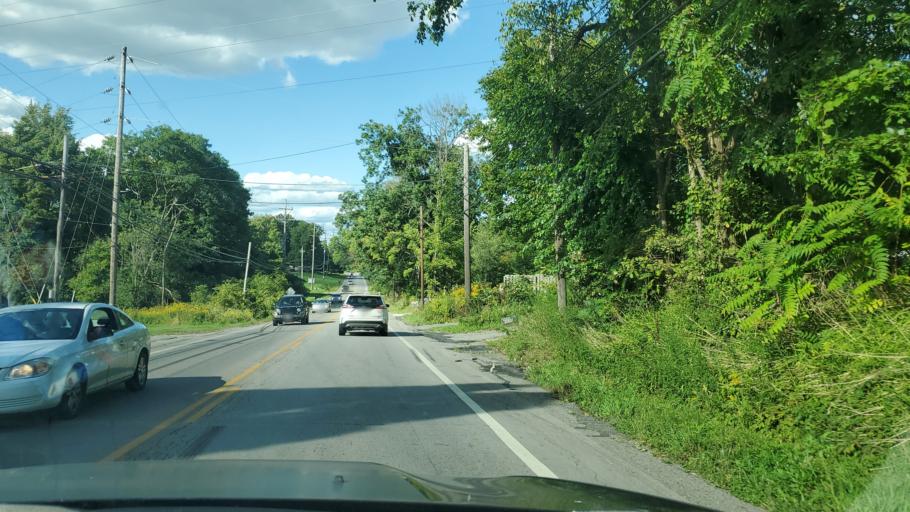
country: US
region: Ohio
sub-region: Trumbull County
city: Mineral Ridge
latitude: 41.1535
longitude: -80.7688
